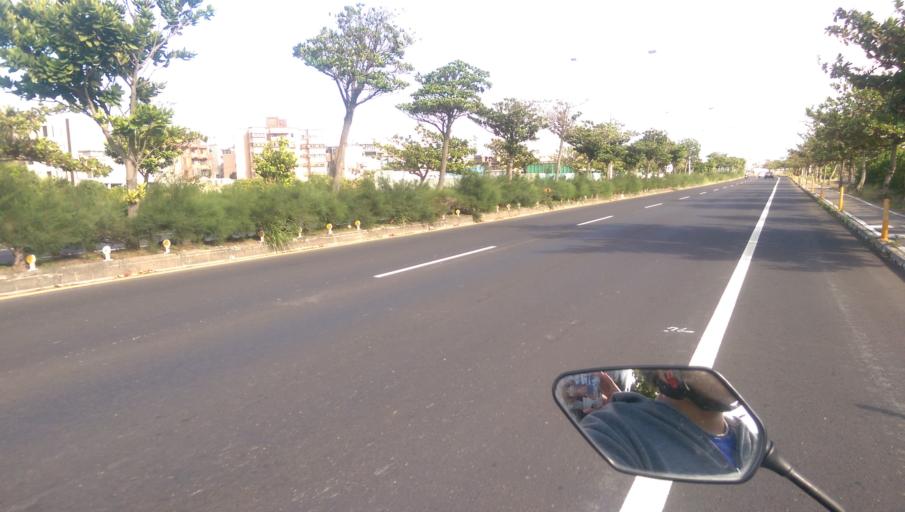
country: TW
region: Taiwan
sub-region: Hsinchu
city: Hsinchu
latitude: 24.8370
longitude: 120.9382
